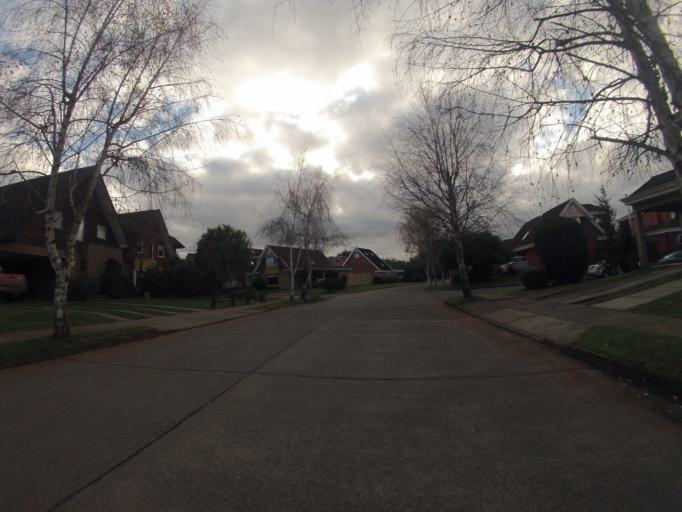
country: CL
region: Araucania
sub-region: Provincia de Cautin
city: Temuco
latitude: -38.7373
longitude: -72.6439
